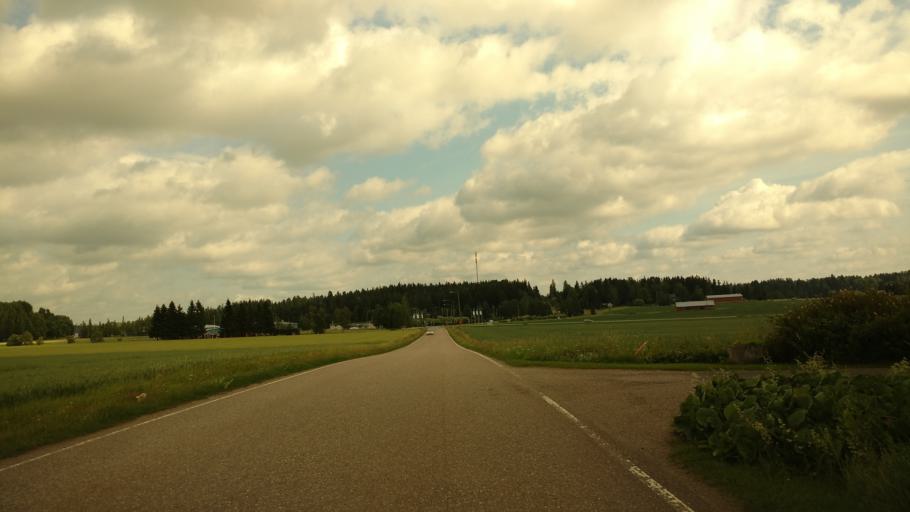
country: FI
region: Haeme
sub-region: Forssa
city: Ypaejae
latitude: 60.7921
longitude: 23.2743
